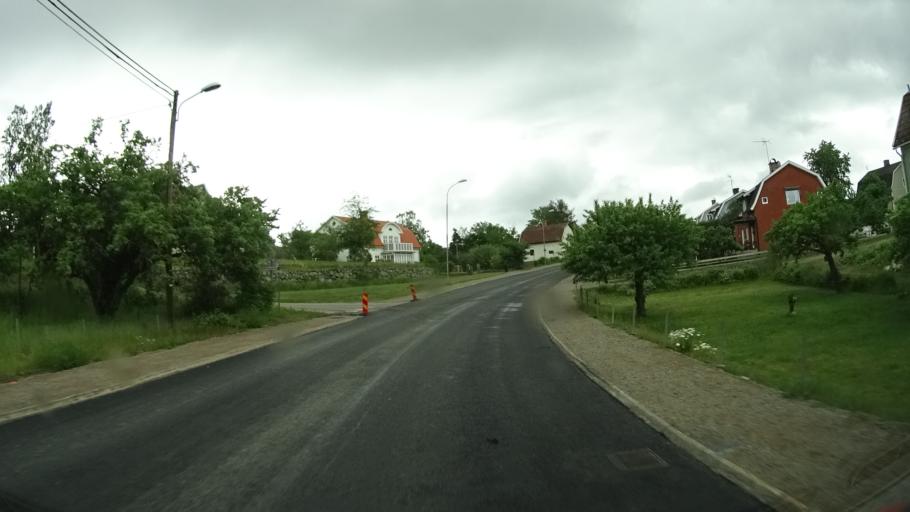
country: SE
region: Kalmar
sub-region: Hogsby Kommun
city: Hoegsby
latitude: 57.4024
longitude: 16.1913
